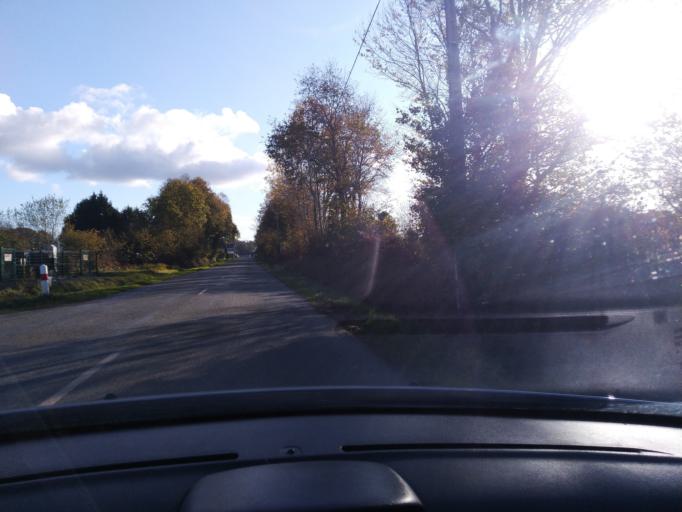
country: FR
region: Brittany
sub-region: Departement des Cotes-d'Armor
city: Plestin-les-Greves
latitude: 48.6124
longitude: -3.6200
